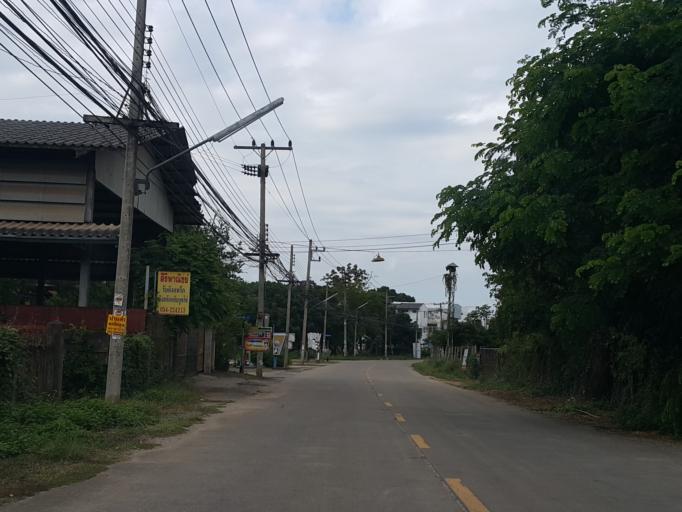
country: TH
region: Lampang
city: Lampang
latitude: 18.2781
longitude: 99.4917
